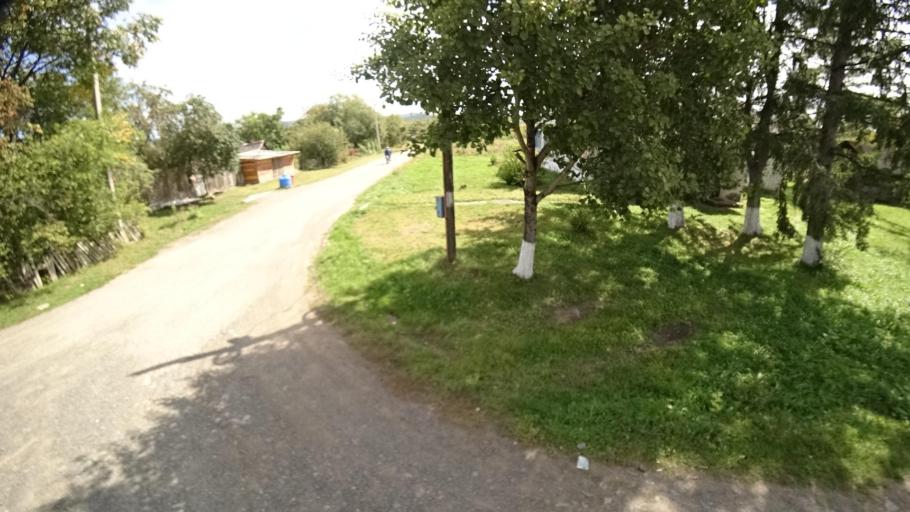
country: RU
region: Primorskiy
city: Yakovlevka
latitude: 44.6432
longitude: 133.5902
